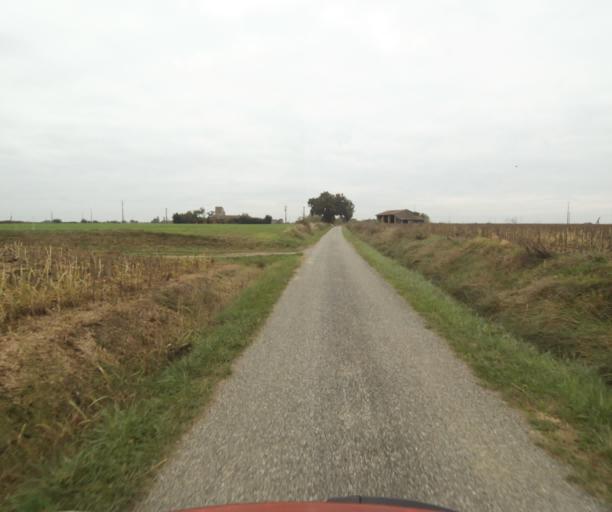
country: FR
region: Midi-Pyrenees
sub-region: Departement de la Haute-Garonne
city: Launac
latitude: 43.8004
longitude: 1.1947
